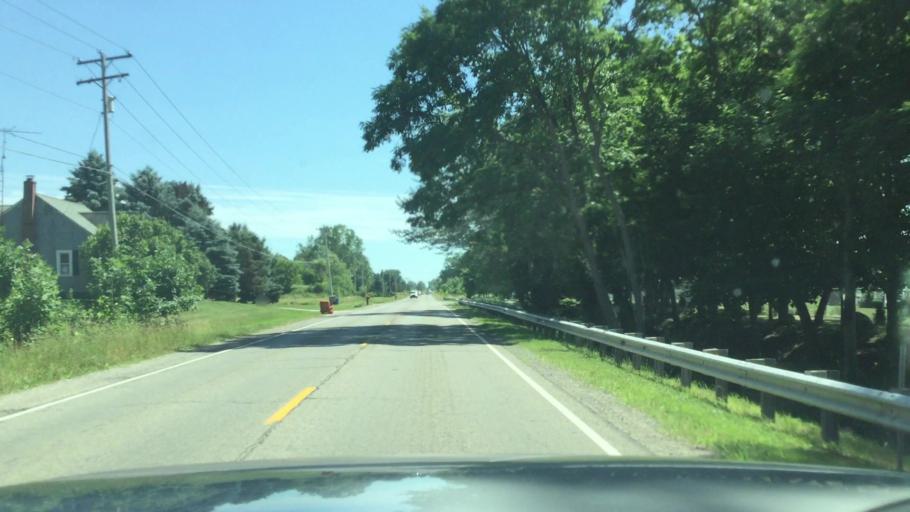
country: US
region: Michigan
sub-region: Genesee County
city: Swartz Creek
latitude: 42.9562
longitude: -83.8111
